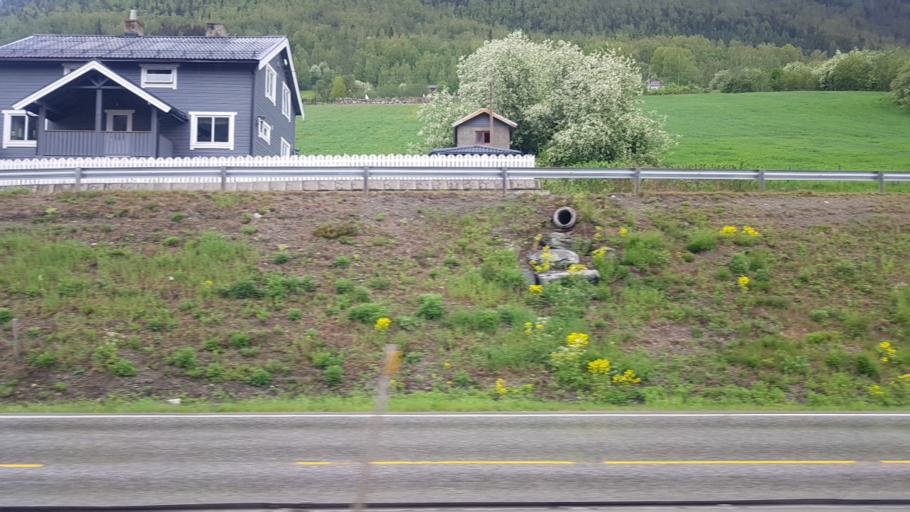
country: NO
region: Oppland
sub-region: Nord-Fron
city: Vinstra
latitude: 61.6658
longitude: 9.6576
